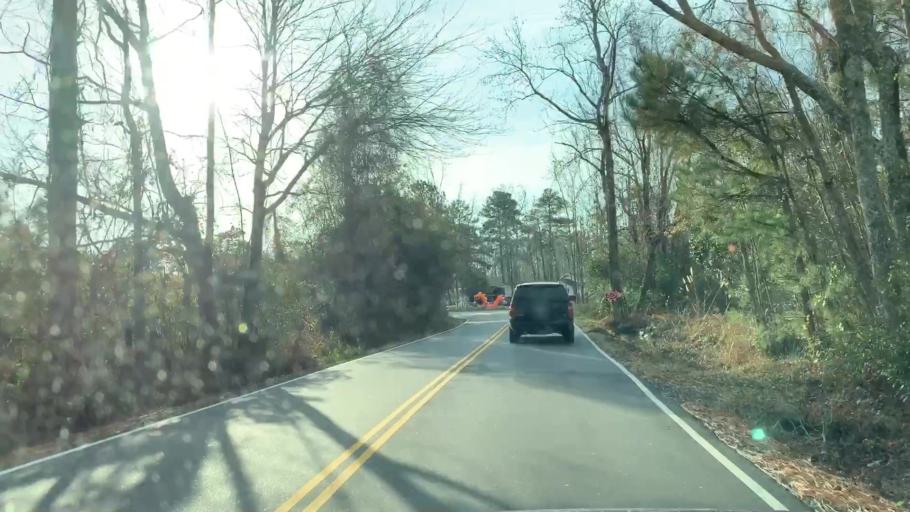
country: US
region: Virginia
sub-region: City of Virginia Beach
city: Virginia Beach
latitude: 36.6932
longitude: -76.0373
